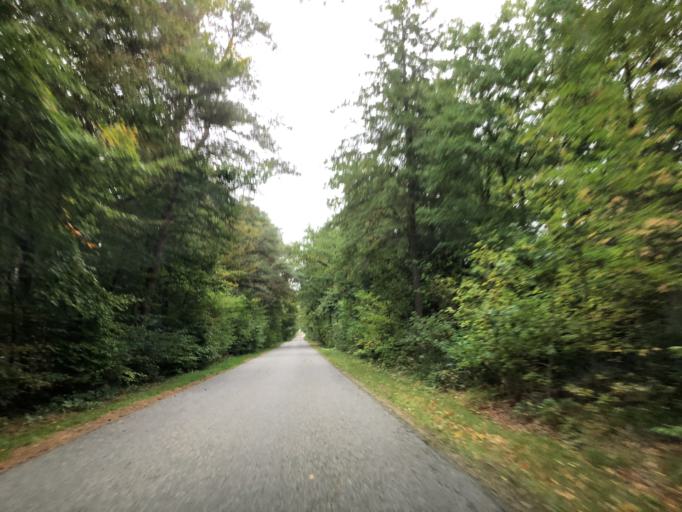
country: DK
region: Central Jutland
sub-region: Viborg Kommune
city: Viborg
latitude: 56.4283
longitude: 9.3681
